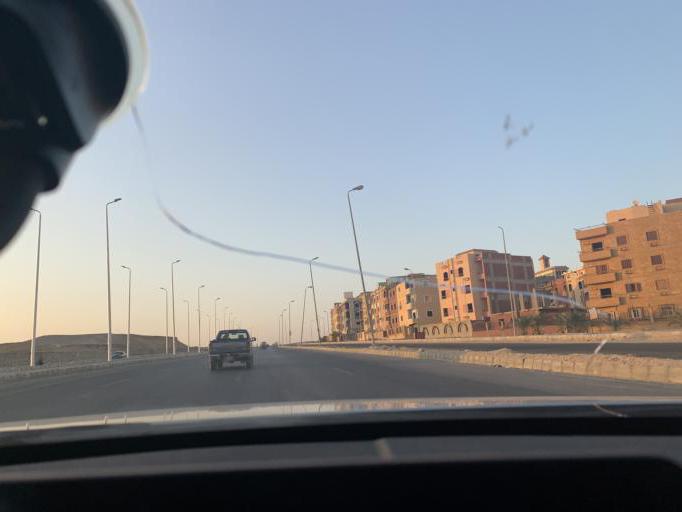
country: EG
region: Muhafazat al Qahirah
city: Halwan
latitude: 29.9811
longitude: 31.4687
